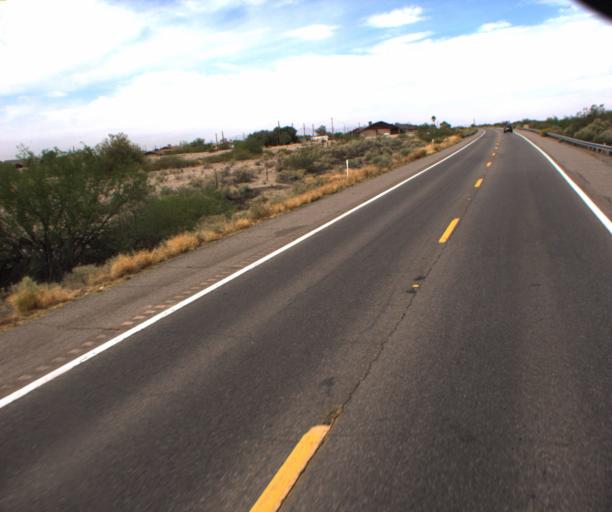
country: US
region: Arizona
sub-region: Pinal County
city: Sacaton
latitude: 33.1187
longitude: -111.7306
